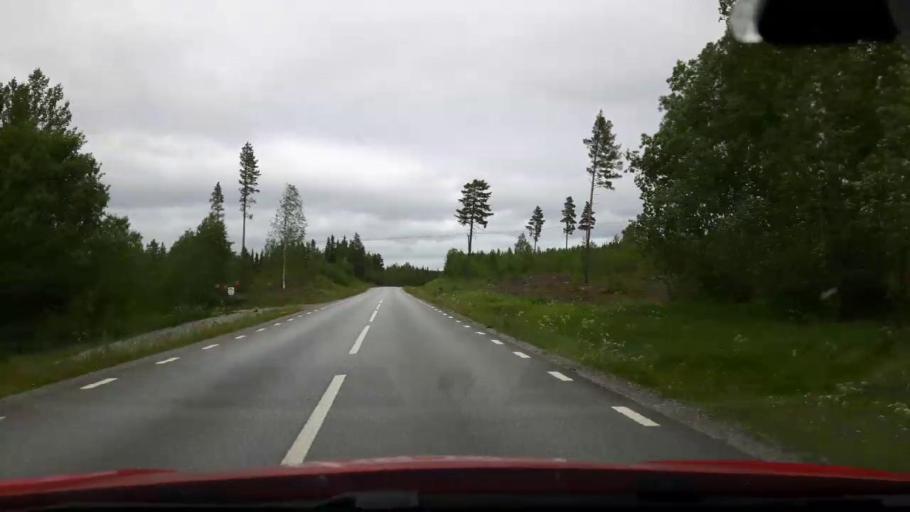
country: SE
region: Jaemtland
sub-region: OEstersunds Kommun
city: Lit
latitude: 63.7222
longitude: 14.7173
